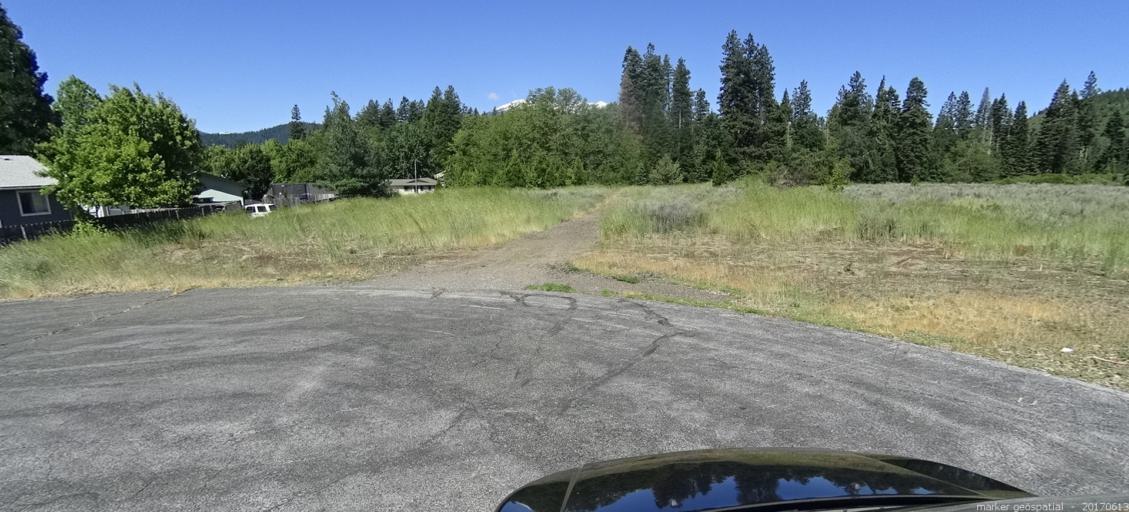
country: US
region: California
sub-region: Siskiyou County
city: Mount Shasta
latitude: 41.3216
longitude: -122.3142
